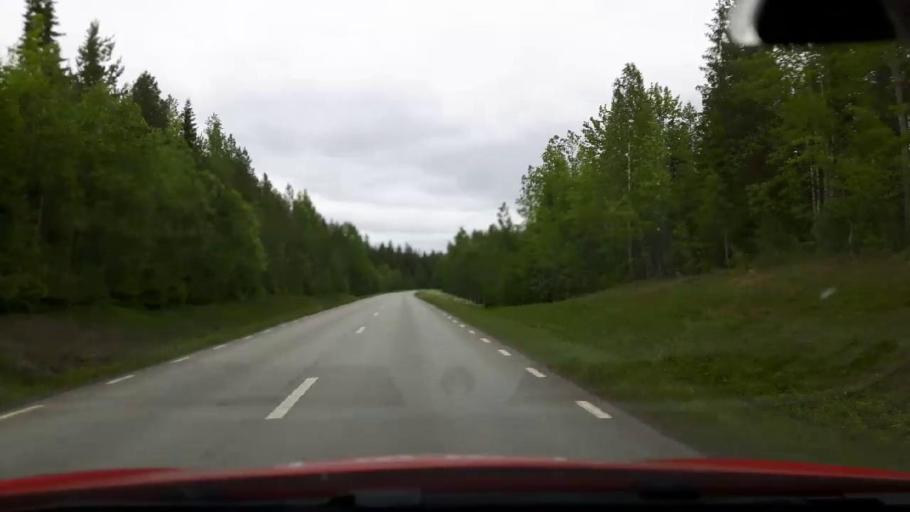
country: SE
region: Jaemtland
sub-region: OEstersunds Kommun
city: Lit
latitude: 63.6750
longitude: 14.6537
